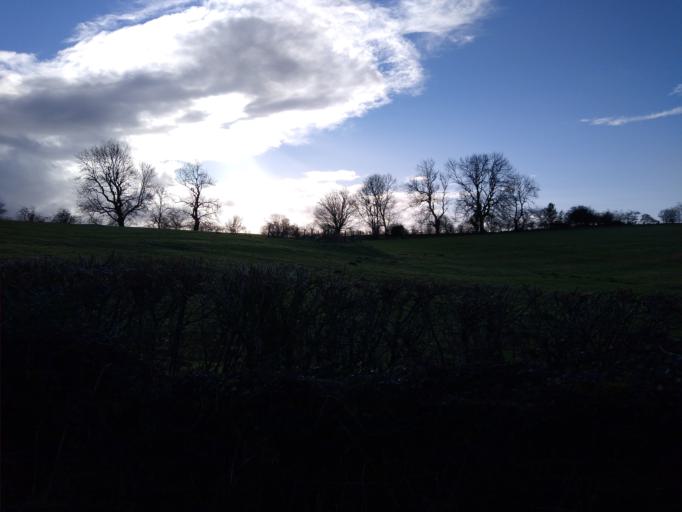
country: GB
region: England
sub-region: Cumbria
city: Cockermouth
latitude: 54.6869
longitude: -3.3683
